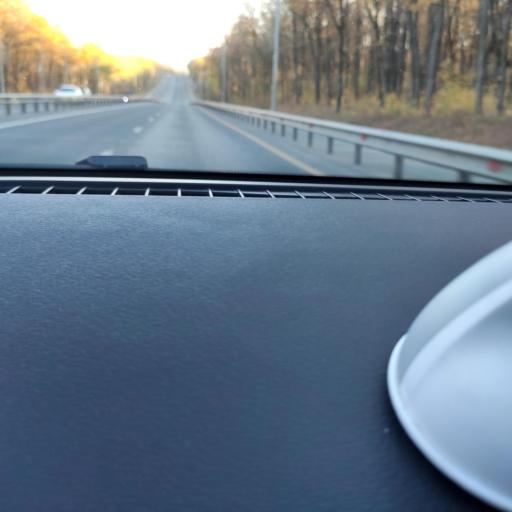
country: RU
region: Samara
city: Petra-Dubrava
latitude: 53.2911
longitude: 50.2476
